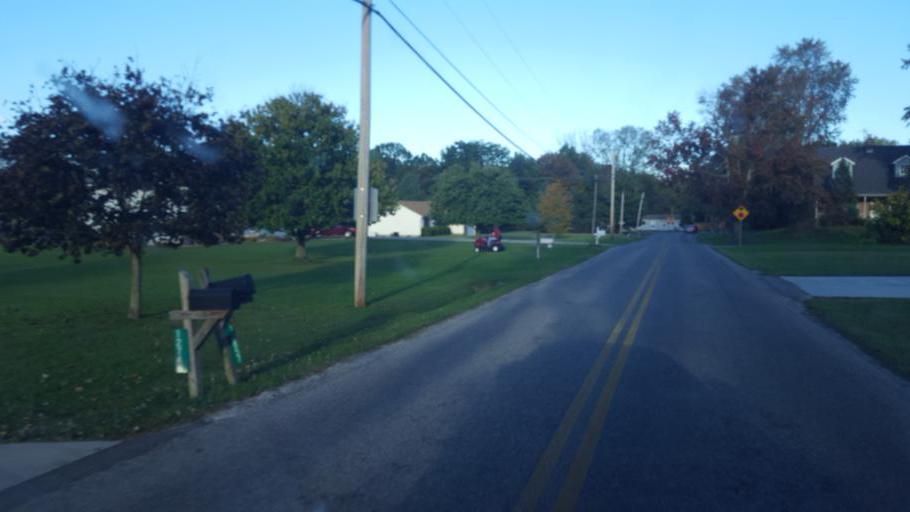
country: US
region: Ohio
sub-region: Licking County
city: Pataskala
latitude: 40.0150
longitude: -82.7291
